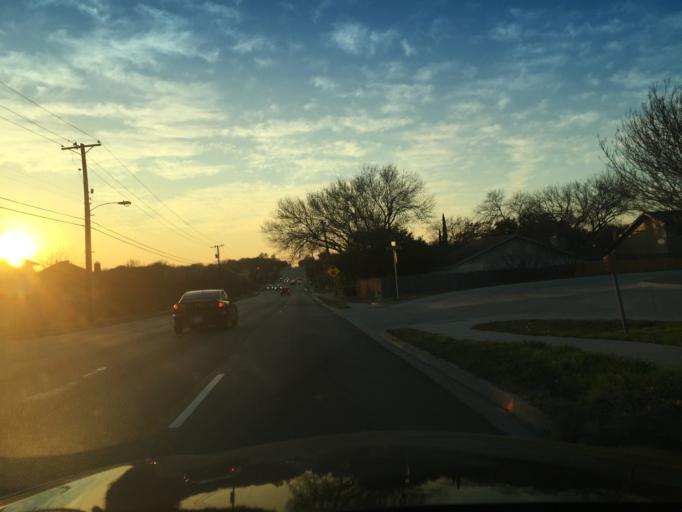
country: US
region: Texas
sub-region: Dallas County
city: Carrollton
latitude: 32.9756
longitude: -96.8946
